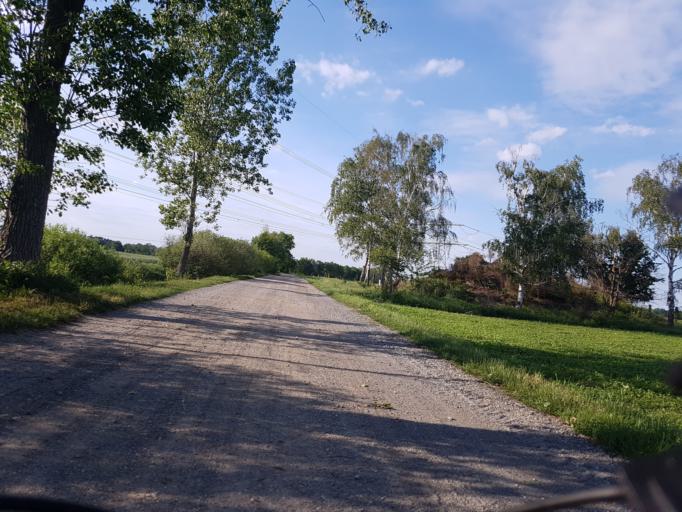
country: DE
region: Brandenburg
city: Merzdorf
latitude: 51.4231
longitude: 13.5267
